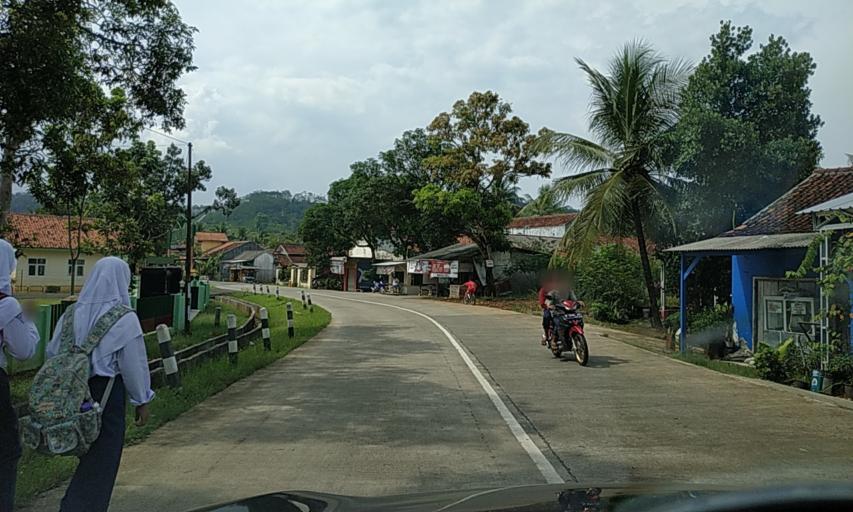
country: ID
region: Central Java
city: Winangun
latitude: -7.3475
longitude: 108.7086
